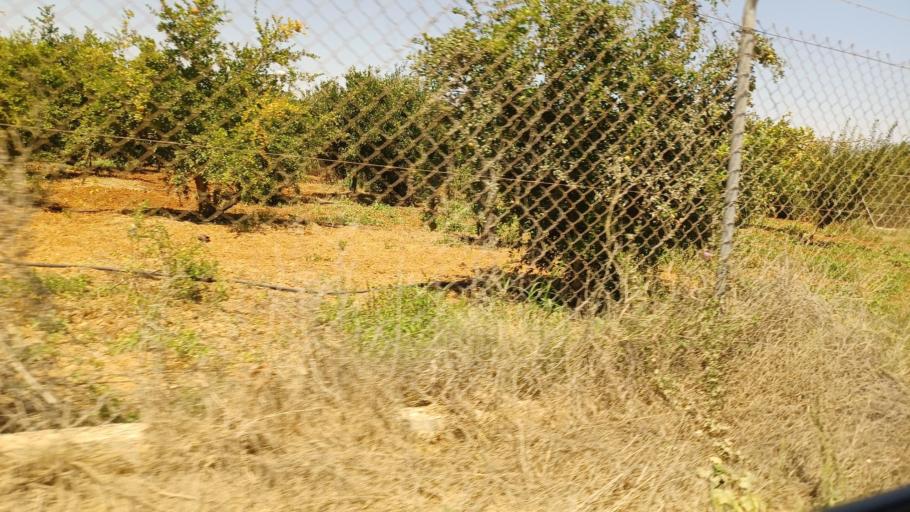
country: CY
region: Ammochostos
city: Acheritou
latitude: 35.0771
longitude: 33.8846
